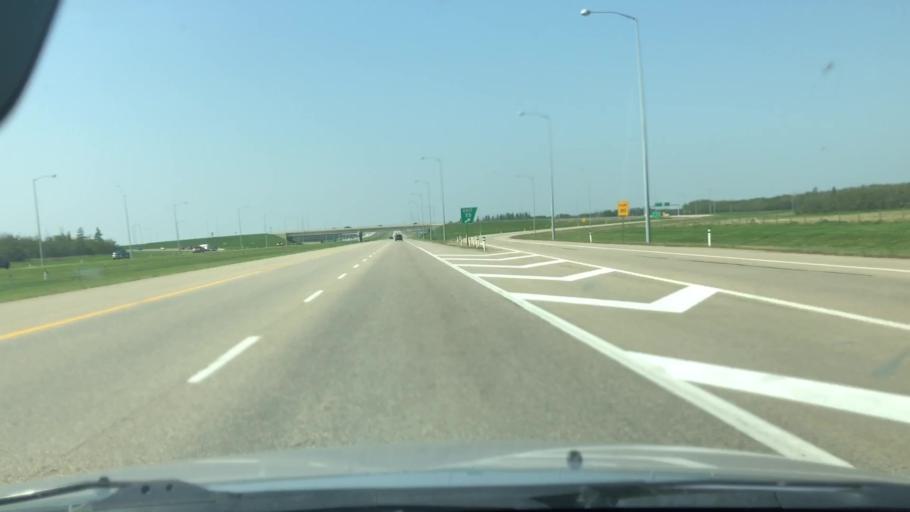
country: CA
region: Alberta
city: St. Albert
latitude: 53.6419
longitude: -113.5371
